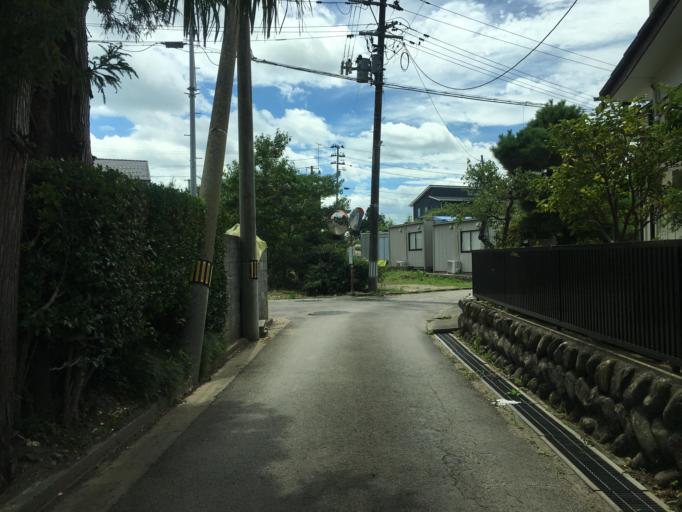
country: JP
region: Miyagi
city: Marumori
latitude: 37.7942
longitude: 140.9173
